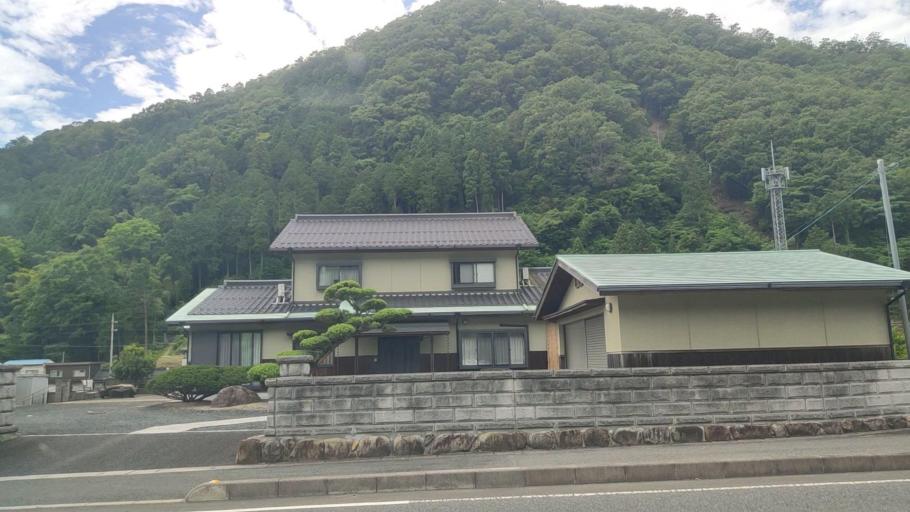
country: JP
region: Hyogo
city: Yamazakicho-nakabirose
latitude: 35.1095
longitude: 134.3267
